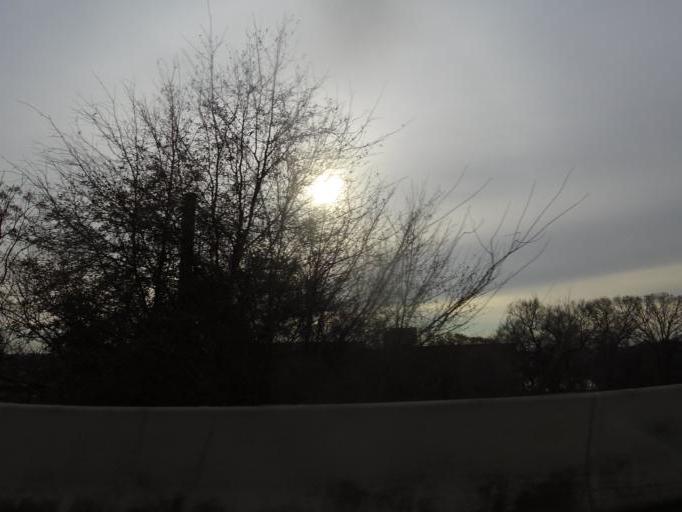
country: US
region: Alabama
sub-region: Montgomery County
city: Montgomery
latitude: 32.3937
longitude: -86.3182
